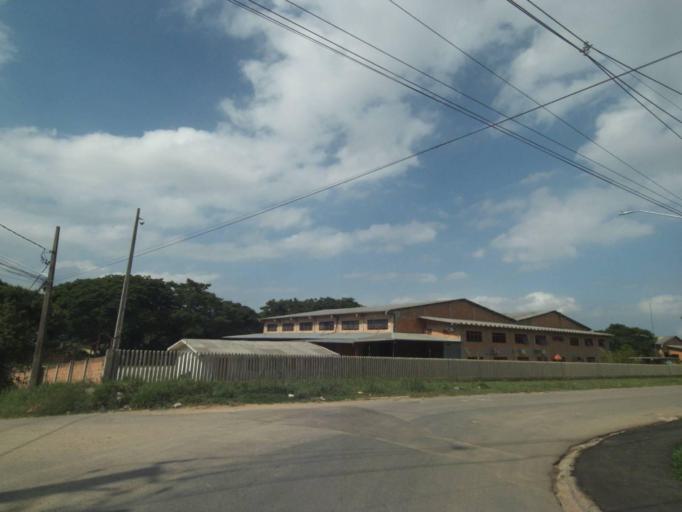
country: BR
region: Parana
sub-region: Araucaria
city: Araucaria
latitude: -25.5049
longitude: -49.3491
